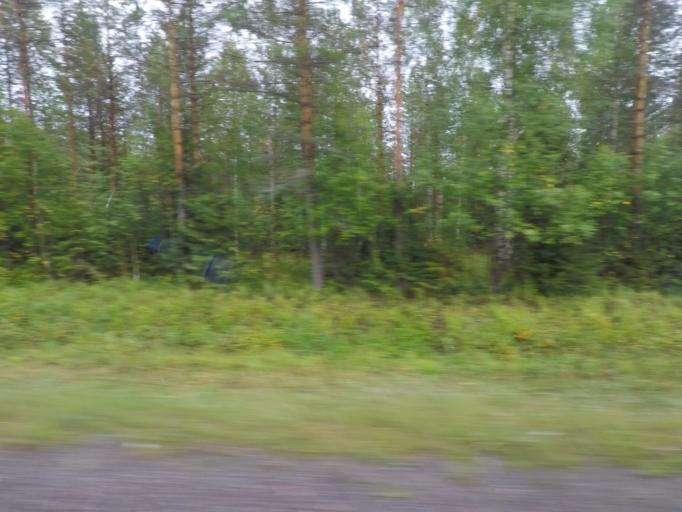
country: FI
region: Southern Savonia
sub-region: Pieksaemaeki
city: Joroinen
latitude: 62.1020
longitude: 27.8324
